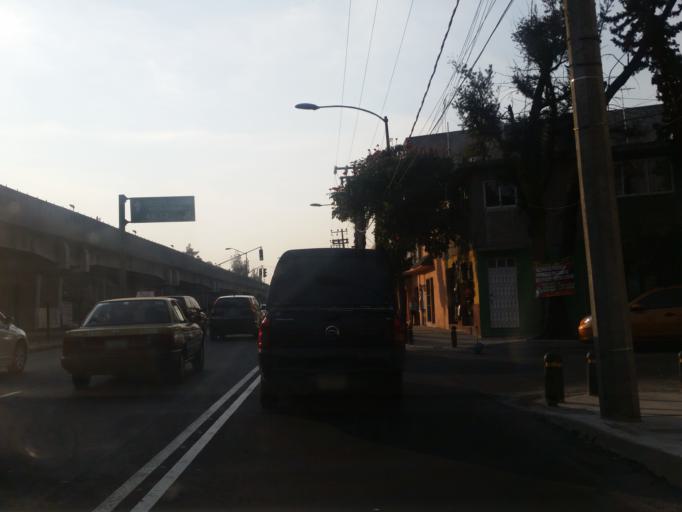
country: MX
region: Mexico City
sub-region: Iztacalco
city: Iztacalco
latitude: 19.4078
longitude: -99.0852
